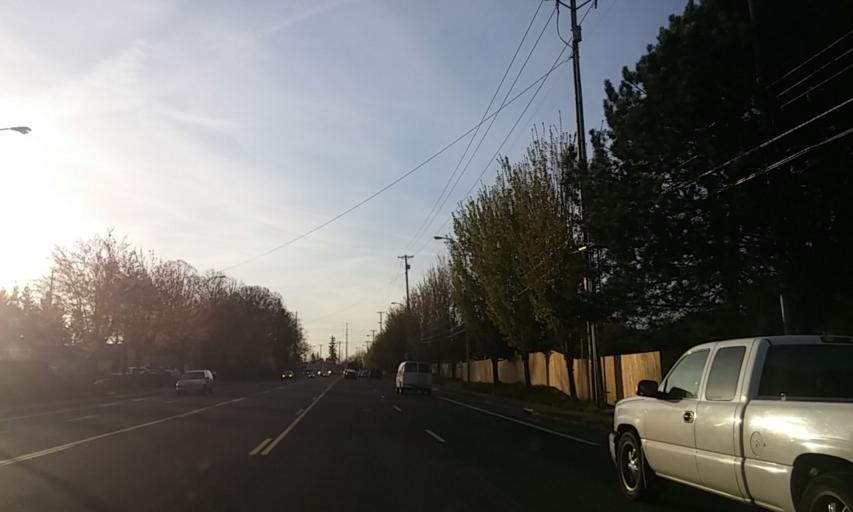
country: US
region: Oregon
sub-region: Washington County
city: Aloha
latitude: 45.5136
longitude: -122.8613
